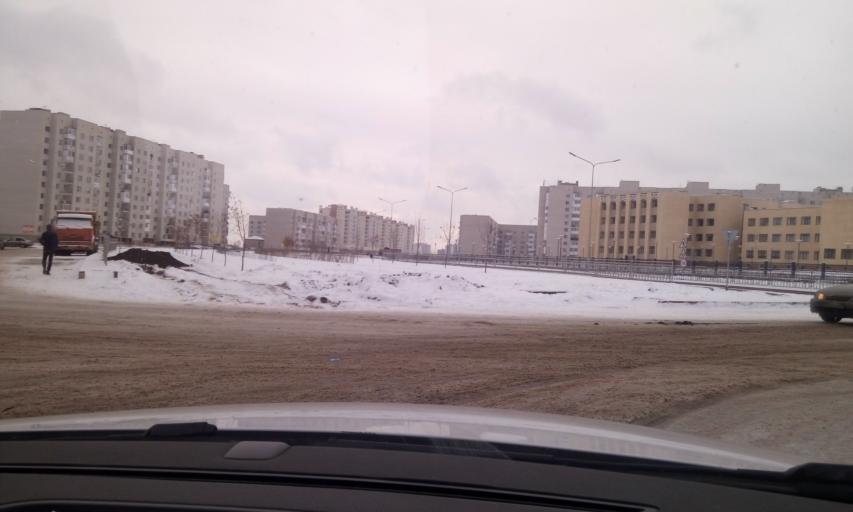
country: KZ
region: Astana Qalasy
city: Astana
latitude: 51.1264
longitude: 71.5045
